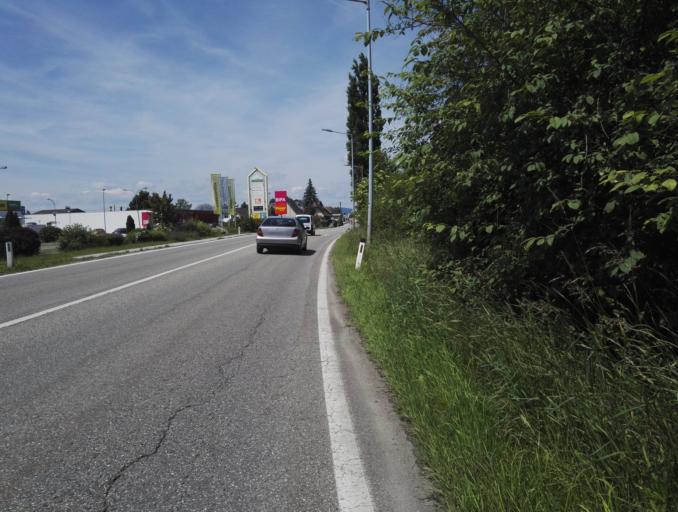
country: AT
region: Styria
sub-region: Politischer Bezirk Graz-Umgebung
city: Kalsdorf bei Graz
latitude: 46.9738
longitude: 15.4713
